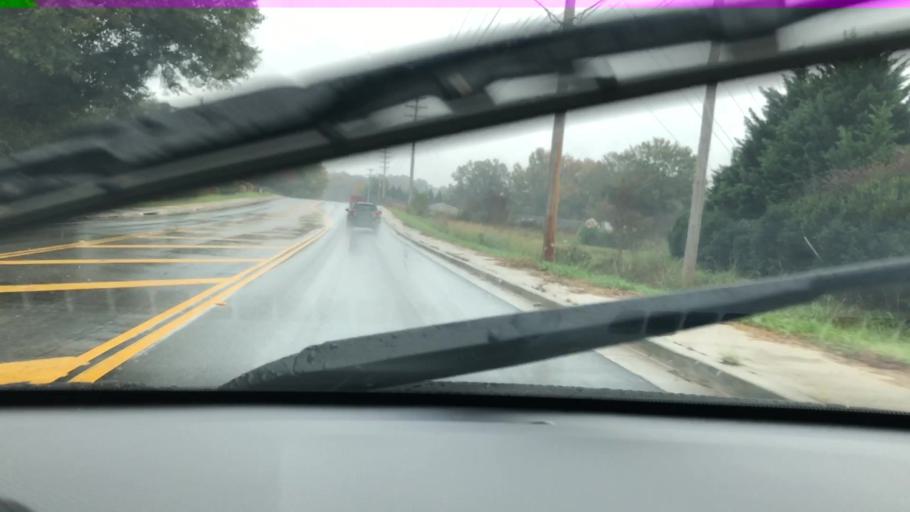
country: US
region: South Carolina
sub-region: Greenville County
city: Five Forks
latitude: 34.8322
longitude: -82.2701
